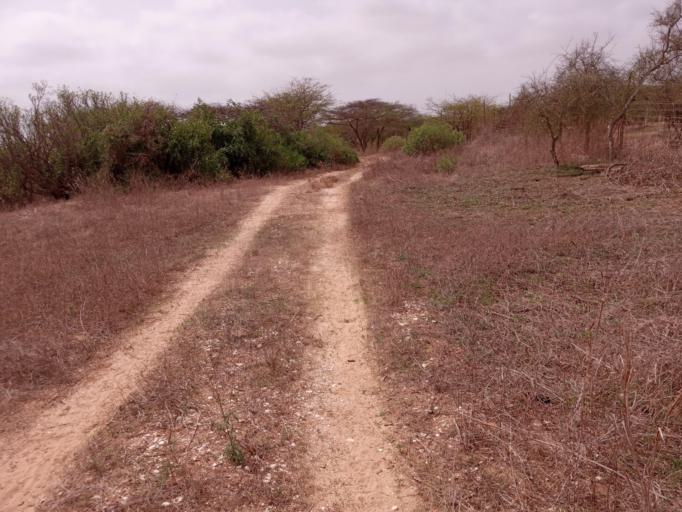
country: SN
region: Saint-Louis
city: Saint-Louis
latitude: 15.9247
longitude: -16.4538
